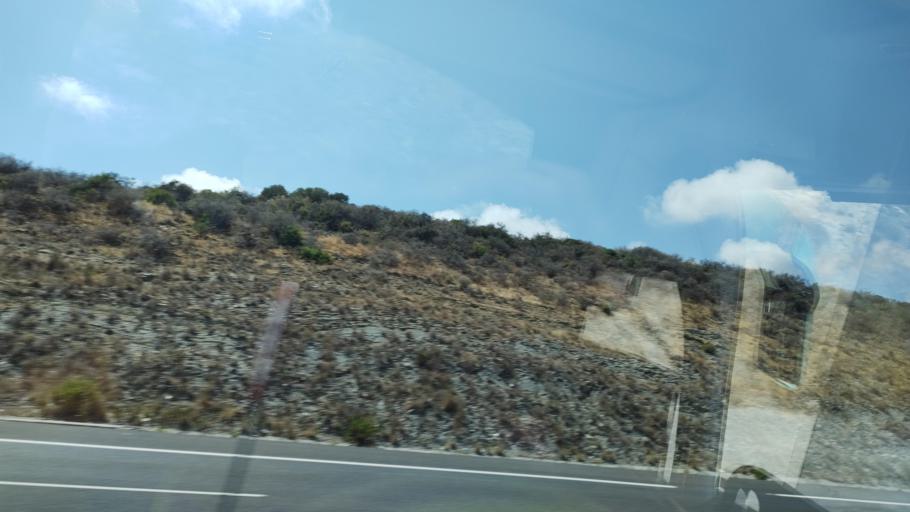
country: ES
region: Andalusia
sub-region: Provincia de Malaga
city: Manilva
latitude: 36.3511
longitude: -5.2714
